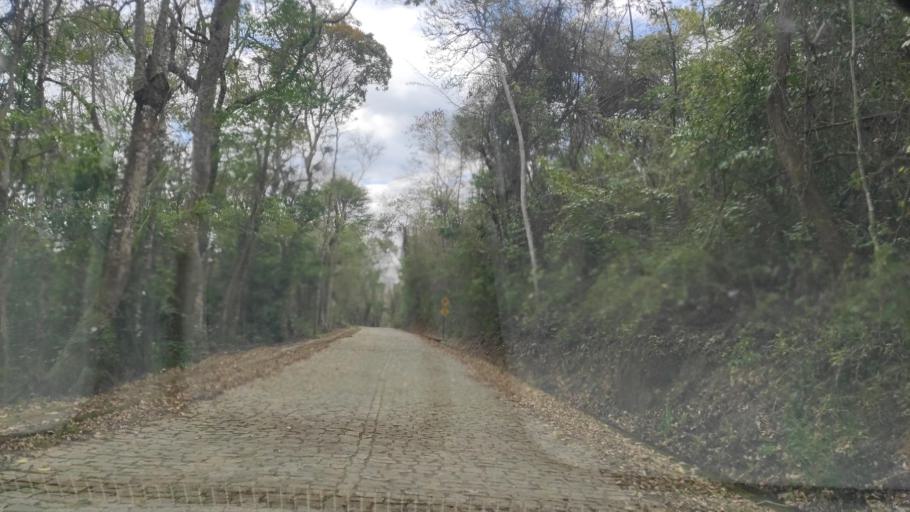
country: BR
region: Espirito Santo
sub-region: Vitoria
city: Vitoria
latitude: -20.3043
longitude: -40.3400
